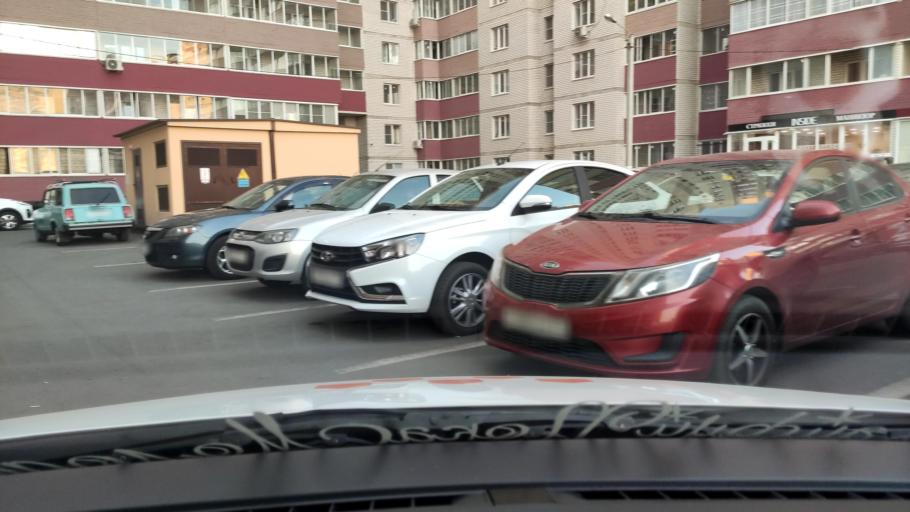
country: RU
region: Voronezj
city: Voronezh
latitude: 51.7123
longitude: 39.1986
